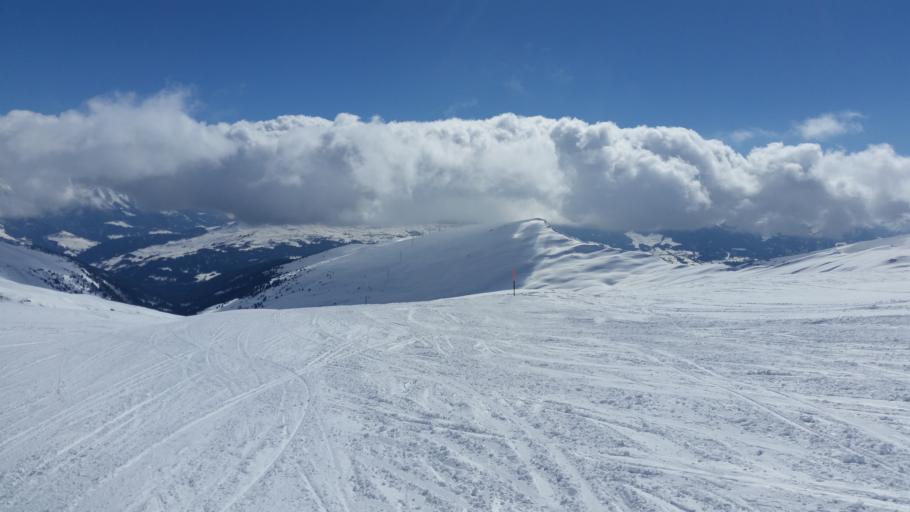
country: CH
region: Grisons
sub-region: Surselva District
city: Ilanz
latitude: 46.8629
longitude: 9.1586
